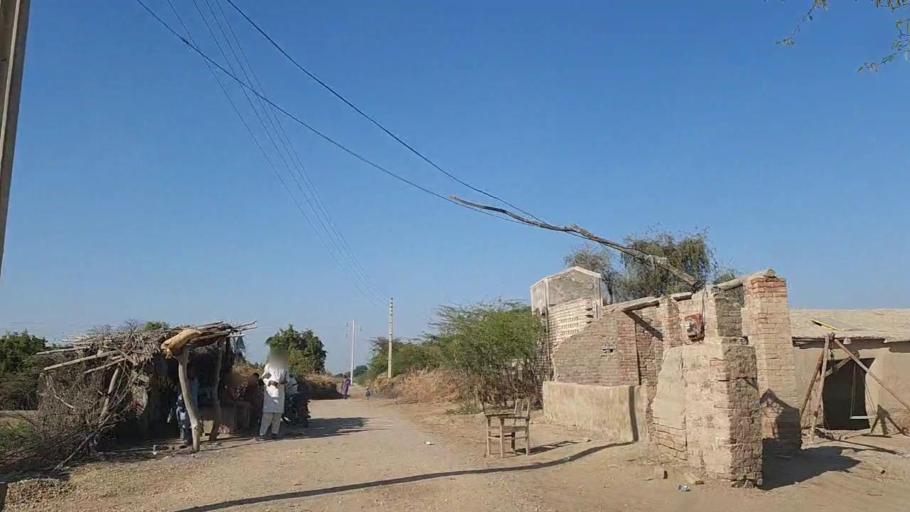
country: PK
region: Sindh
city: Samaro
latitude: 25.3732
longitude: 69.4025
